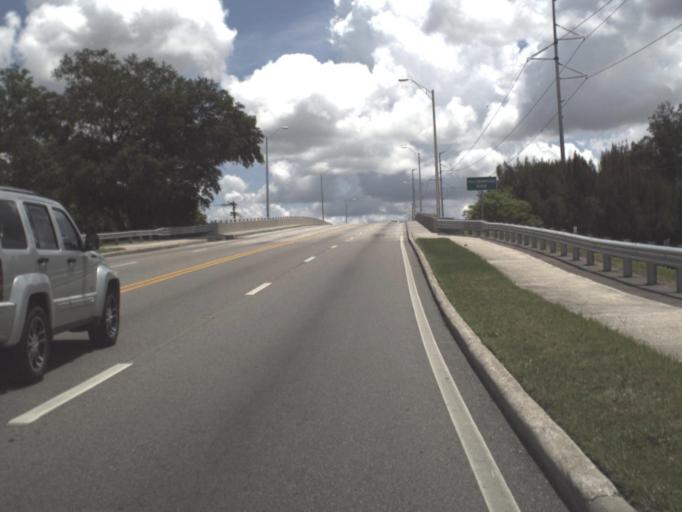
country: US
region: Florida
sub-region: Hillsborough County
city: Tampa
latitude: 27.9814
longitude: -82.4776
